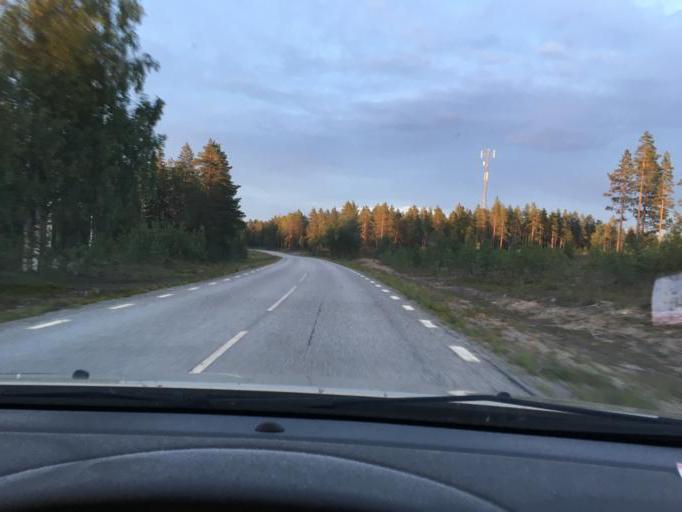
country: SE
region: Norrbotten
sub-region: Kalix Kommun
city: Toere
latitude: 66.0524
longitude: 22.4867
